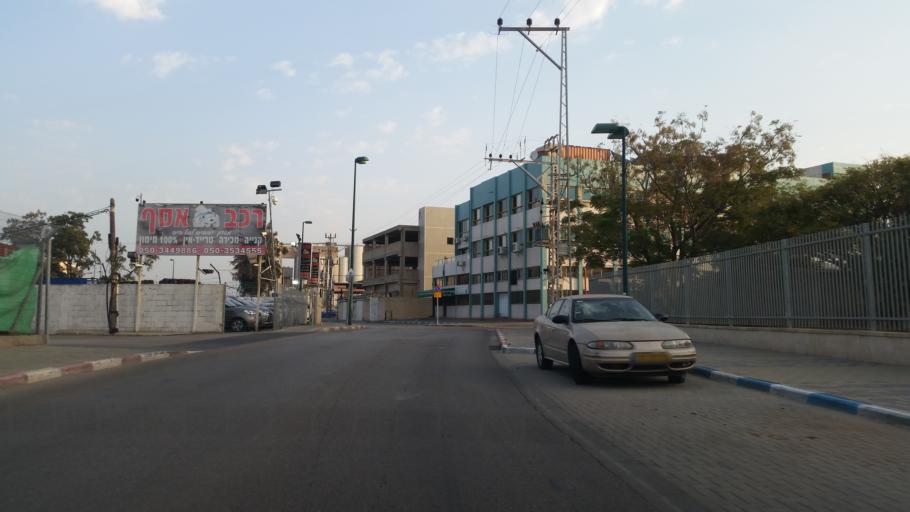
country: IL
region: Central District
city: Netanya
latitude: 32.3169
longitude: 34.8717
